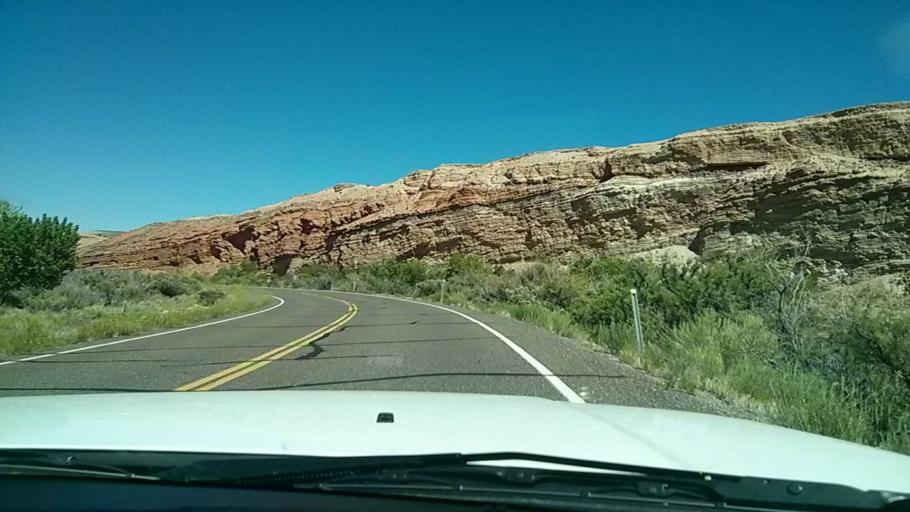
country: US
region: Utah
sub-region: Wayne County
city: Loa
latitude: 38.2841
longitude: -111.1491
